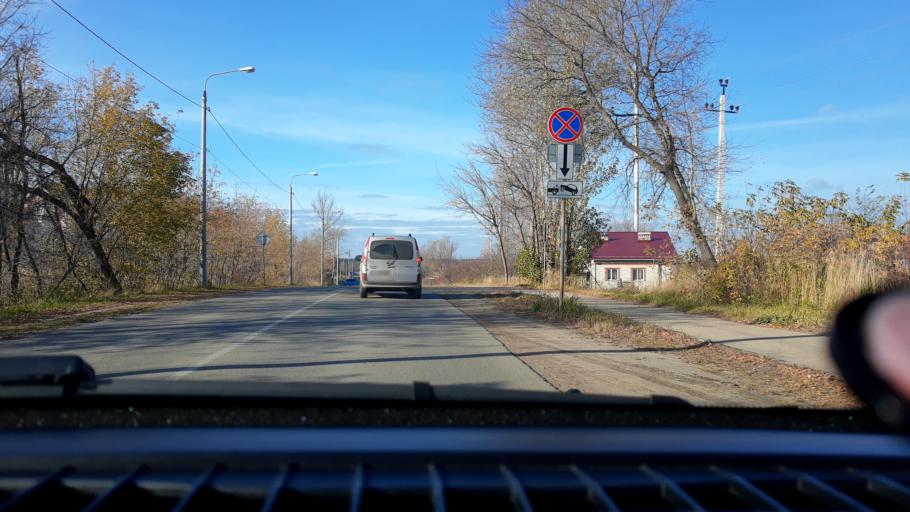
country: RU
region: Nizjnij Novgorod
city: Kstovo
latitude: 56.1630
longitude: 44.1981
